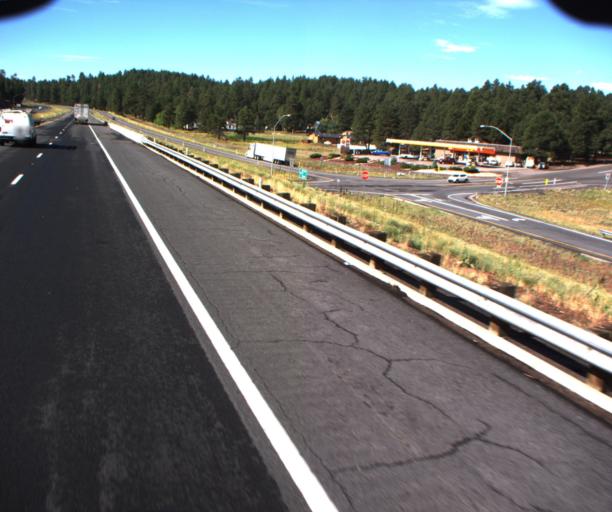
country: US
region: Arizona
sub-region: Coconino County
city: Kachina Village
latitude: 35.0908
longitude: -111.6859
